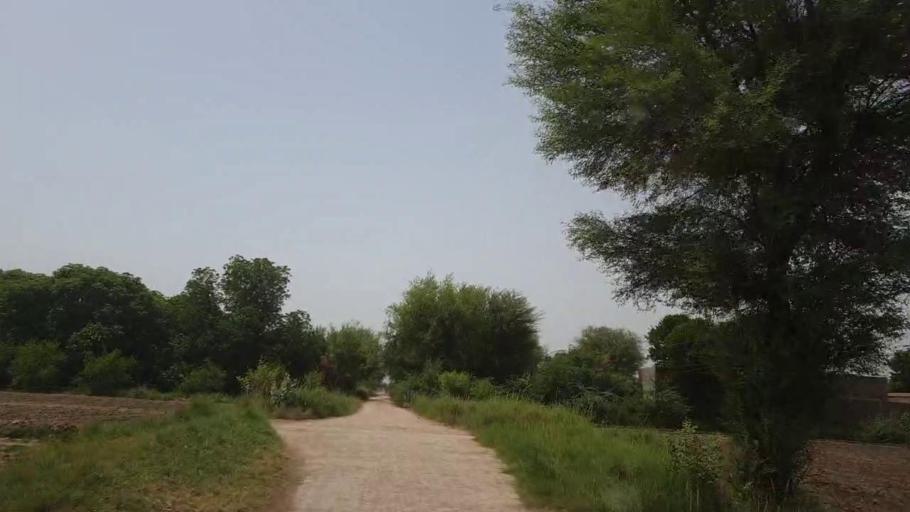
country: PK
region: Sindh
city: Sakrand
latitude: 26.0735
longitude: 68.2667
